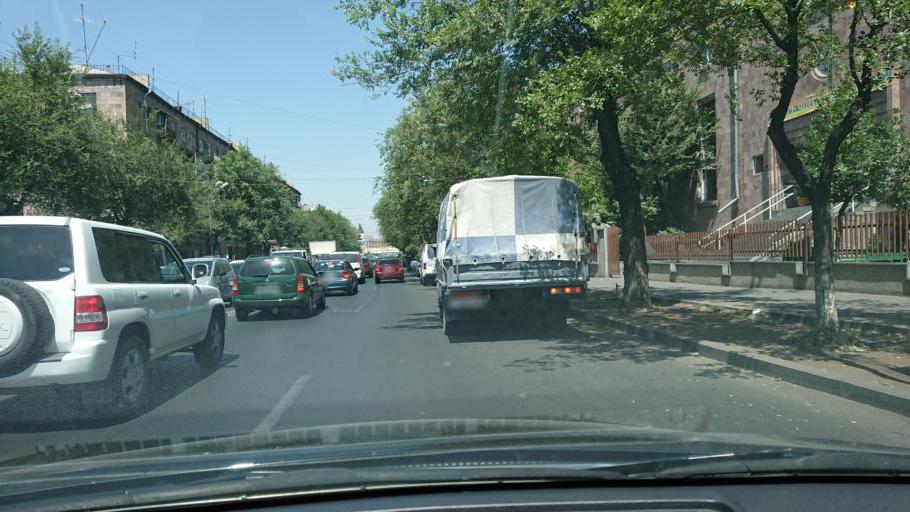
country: AM
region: Yerevan
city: Yerevan
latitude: 40.2032
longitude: 44.4985
